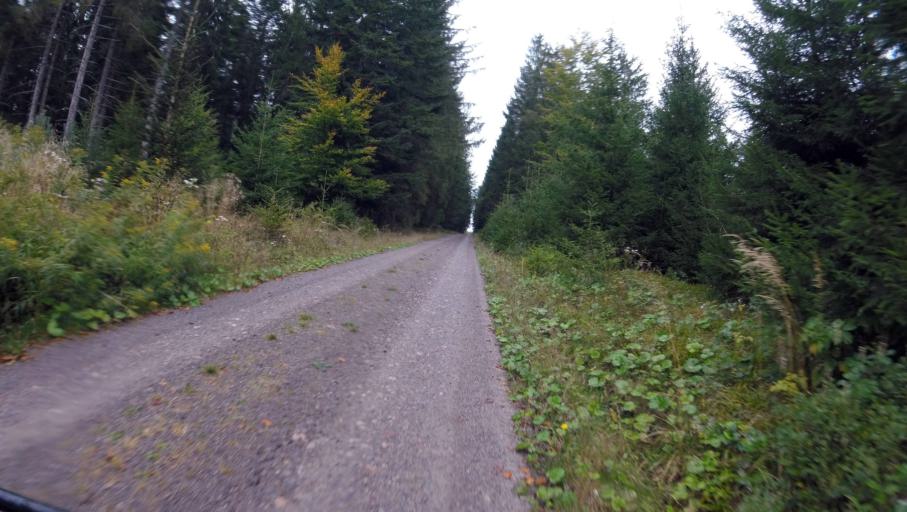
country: DE
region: Baden-Wuerttemberg
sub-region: Karlsruhe Region
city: Forbach
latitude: 48.6561
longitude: 8.4045
